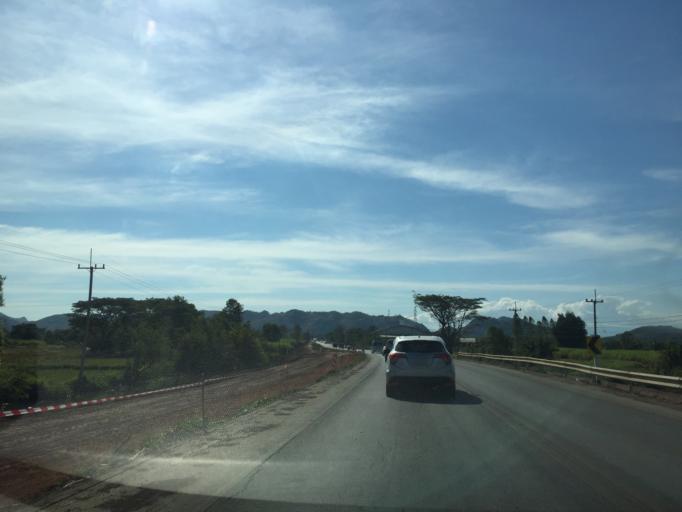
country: TH
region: Loei
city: Wang Saphung
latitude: 17.2989
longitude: 101.8576
